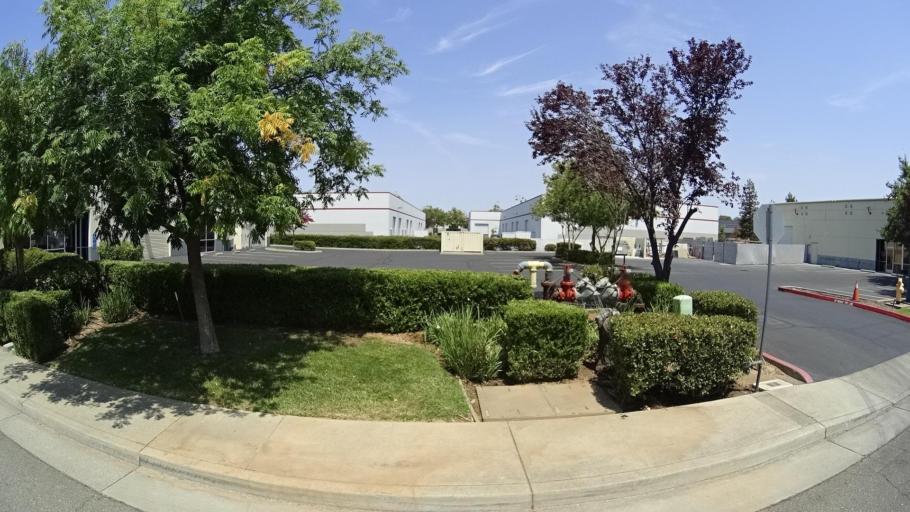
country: US
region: California
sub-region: Placer County
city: Rocklin
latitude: 38.8063
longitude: -121.2187
